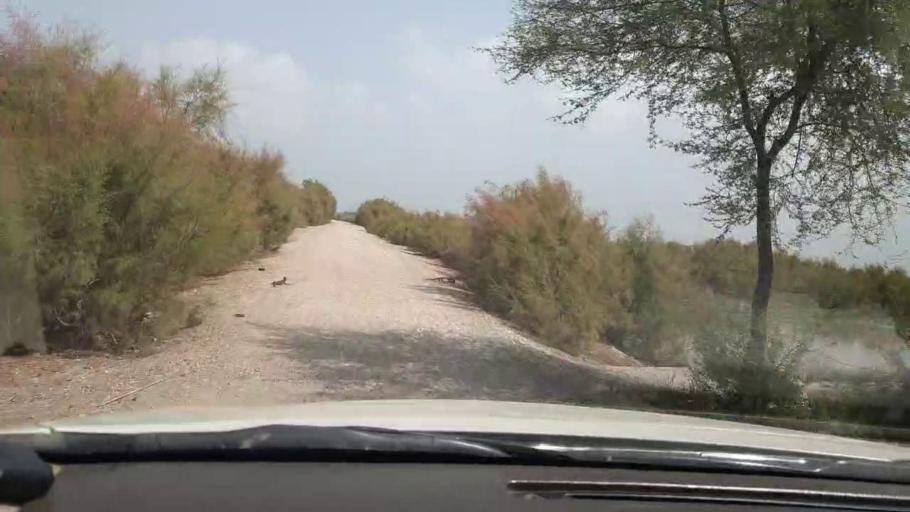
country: PK
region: Sindh
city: Garhi Yasin
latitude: 28.0006
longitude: 68.5408
